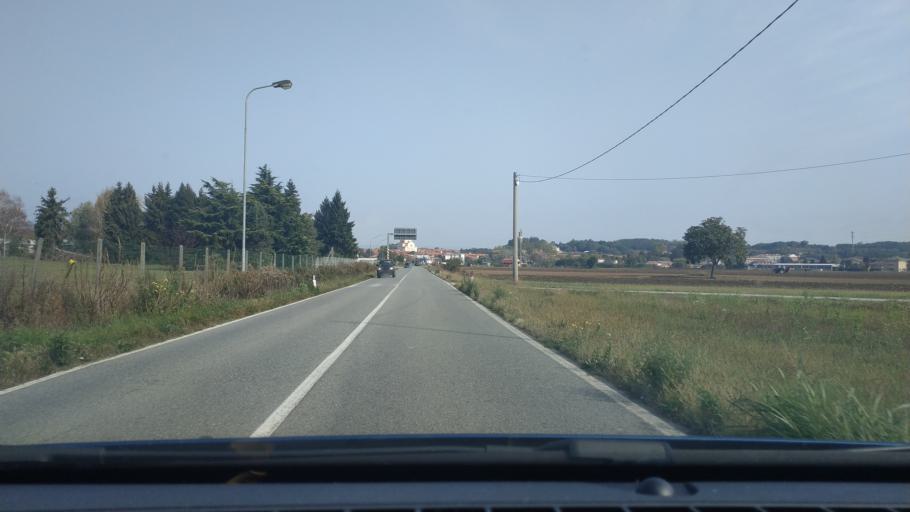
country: IT
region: Piedmont
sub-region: Provincia di Torino
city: Scarmagno
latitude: 45.3816
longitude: 7.8591
